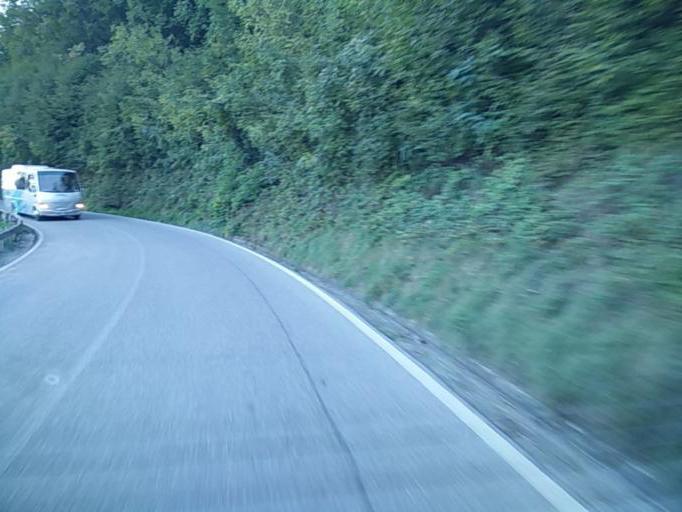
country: IT
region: Lombardy
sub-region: Provincia di Brescia
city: Gargnano
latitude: 45.6886
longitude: 10.6481
